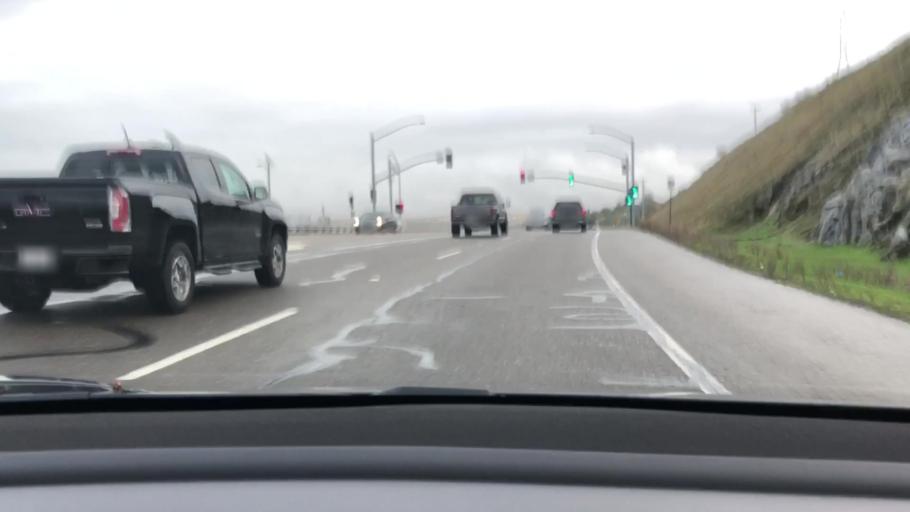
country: US
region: California
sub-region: Sacramento County
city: Folsom
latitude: 38.7017
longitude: -121.1480
